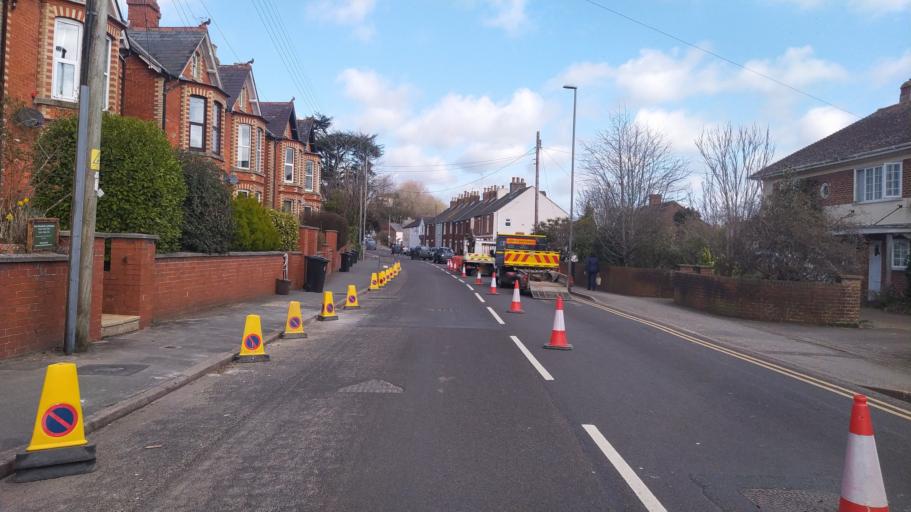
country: GB
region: England
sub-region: Dorset
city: Bridport
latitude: 50.7403
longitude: -2.7451
